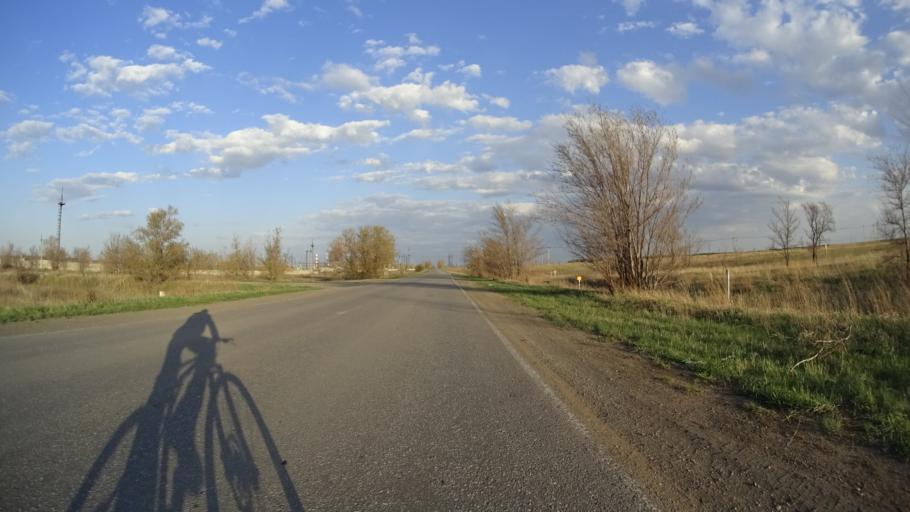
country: RU
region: Chelyabinsk
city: Troitsk
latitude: 54.0605
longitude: 61.5779
